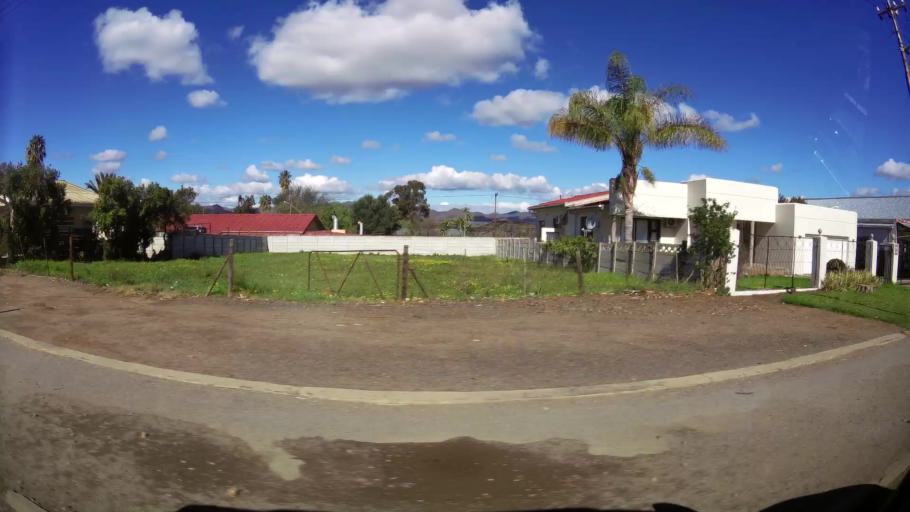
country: ZA
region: Western Cape
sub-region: Cape Winelands District Municipality
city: Ashton
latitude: -33.8350
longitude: 20.0514
